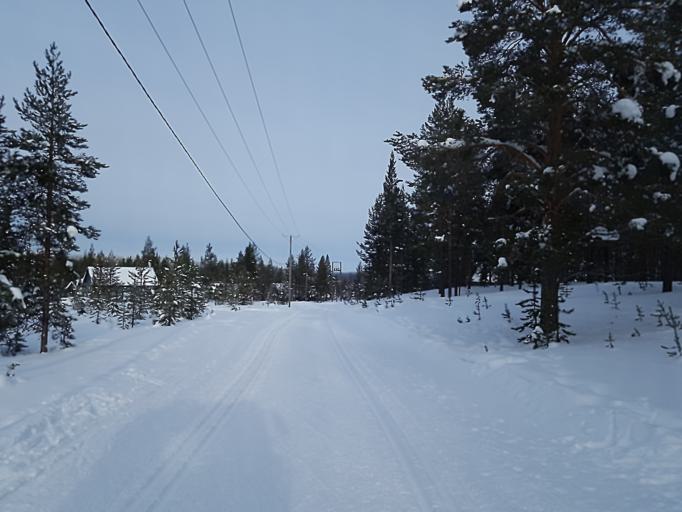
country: FI
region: Lapland
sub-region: Tunturi-Lappi
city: Kolari
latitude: 67.5958
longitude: 24.1599
